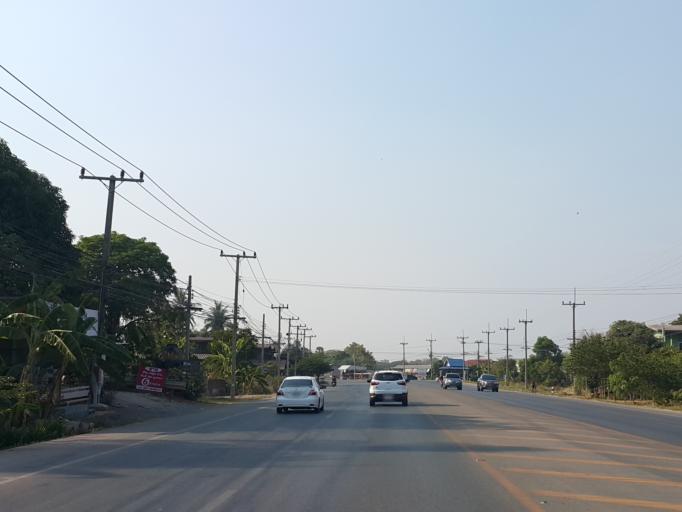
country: TH
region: Phitsanulok
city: Phitsanulok
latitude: 16.9254
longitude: 100.2334
